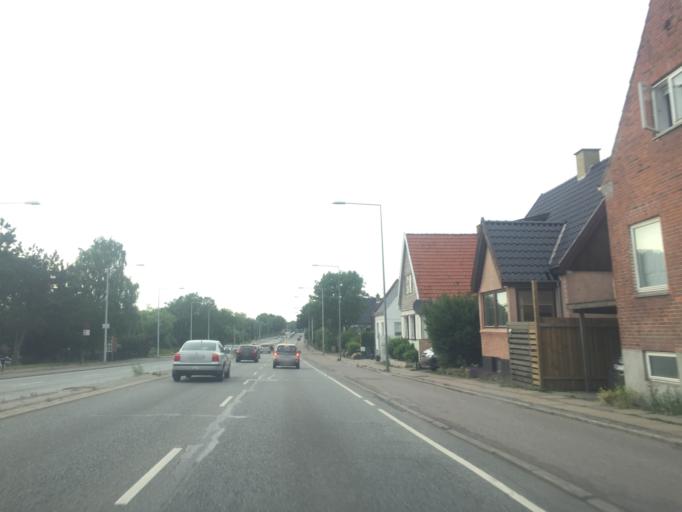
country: DK
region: Capital Region
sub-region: Kobenhavn
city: Vanlose
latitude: 55.7100
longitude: 12.5079
